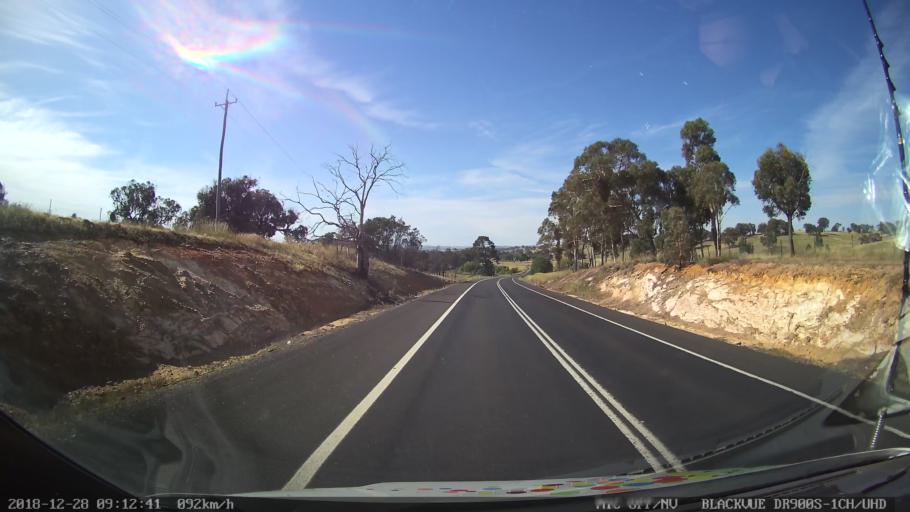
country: AU
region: New South Wales
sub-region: Upper Lachlan Shire
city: Crookwell
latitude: -34.2586
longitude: 149.3429
